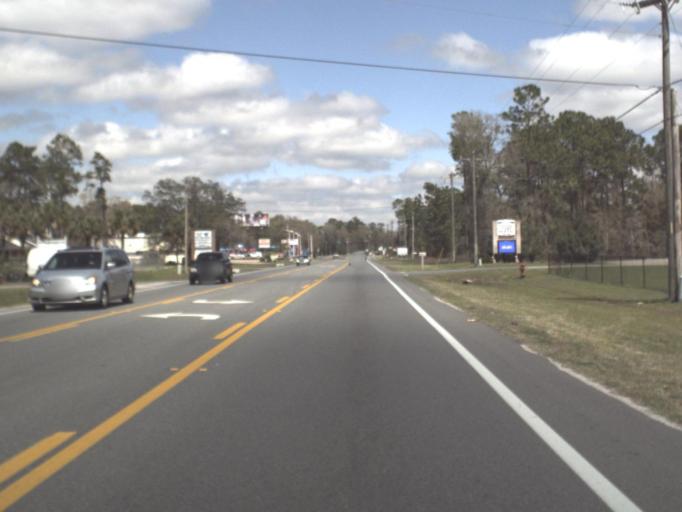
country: US
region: Florida
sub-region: Wakulla County
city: Crawfordville
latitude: 30.2124
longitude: -84.3641
